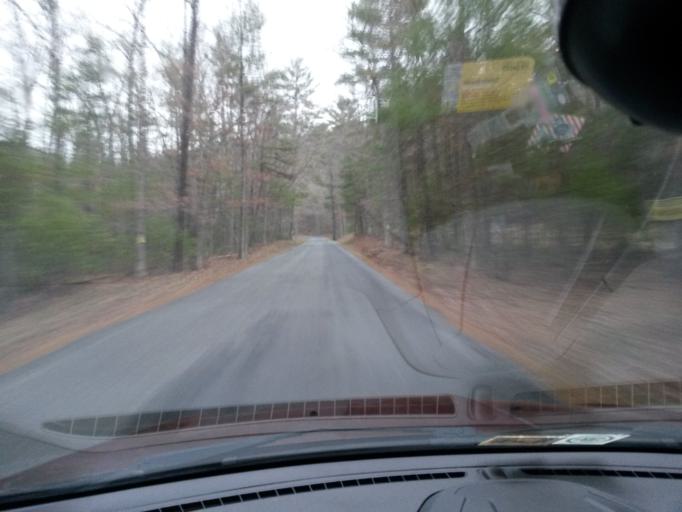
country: US
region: Virginia
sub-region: Bath County
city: Warm Springs
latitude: 37.9954
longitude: -79.7113
